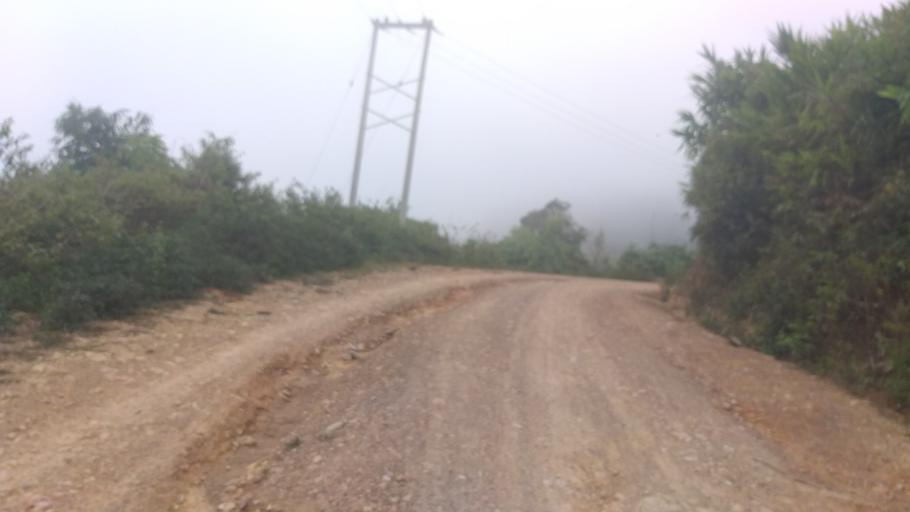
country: LA
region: Phongsali
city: Khoa
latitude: 21.2917
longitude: 102.6410
